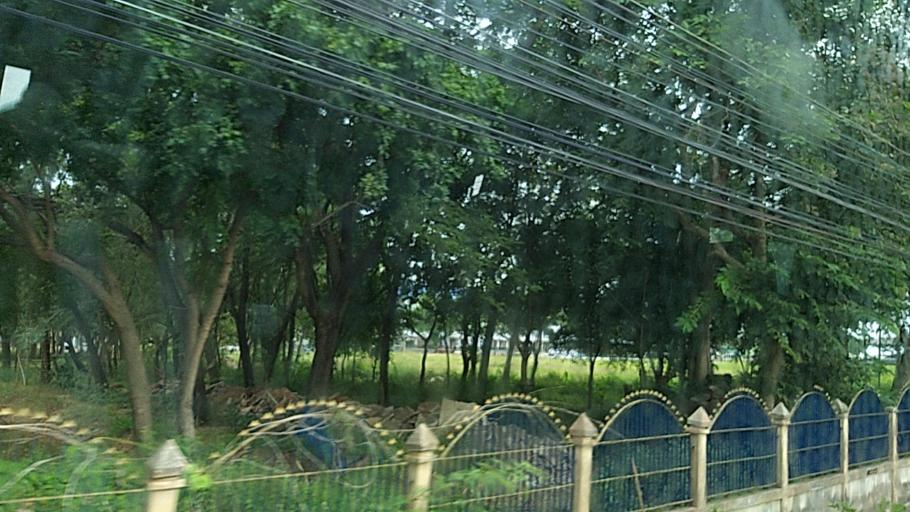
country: TH
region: Maha Sarakham
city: Kantharawichai
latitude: 16.3264
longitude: 103.2942
